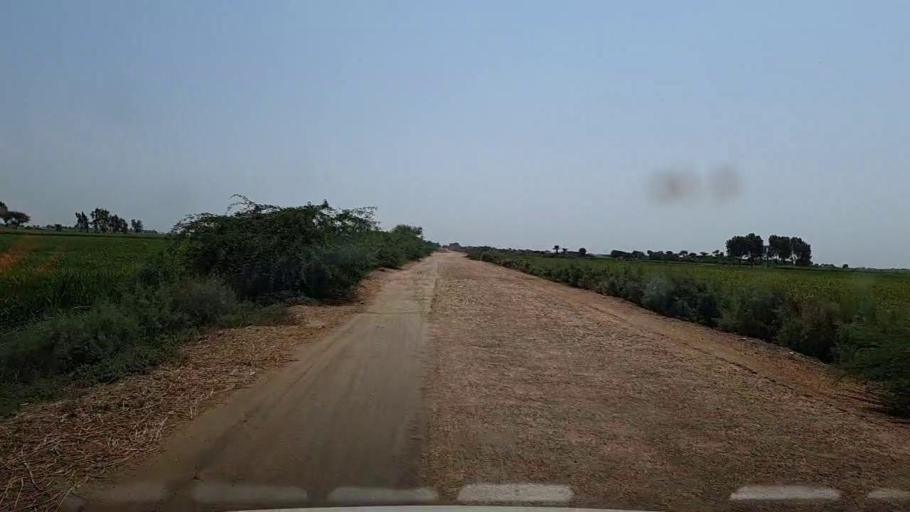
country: PK
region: Sindh
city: Mirpur Batoro
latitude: 24.6267
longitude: 68.4522
